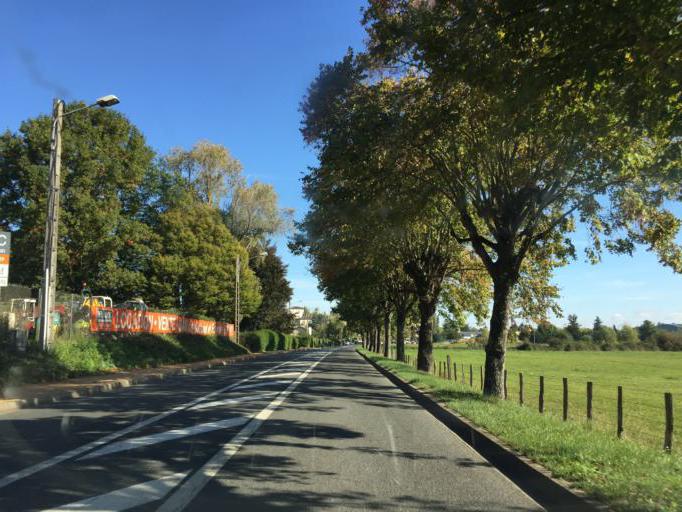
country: FR
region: Rhone-Alpes
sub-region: Departement du Rhone
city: Belleville
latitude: 46.1001
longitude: 4.7330
